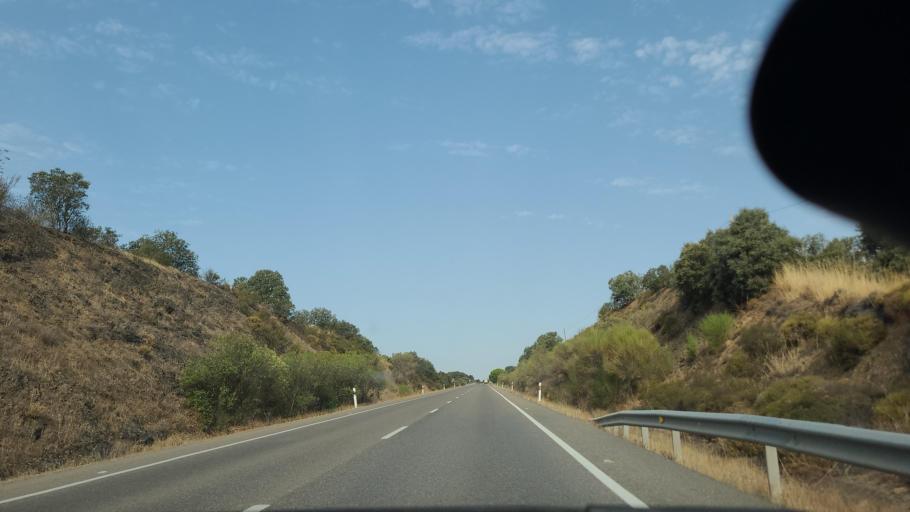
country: ES
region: Andalusia
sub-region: Province of Cordoba
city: Espiel
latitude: 38.1895
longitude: -5.0854
